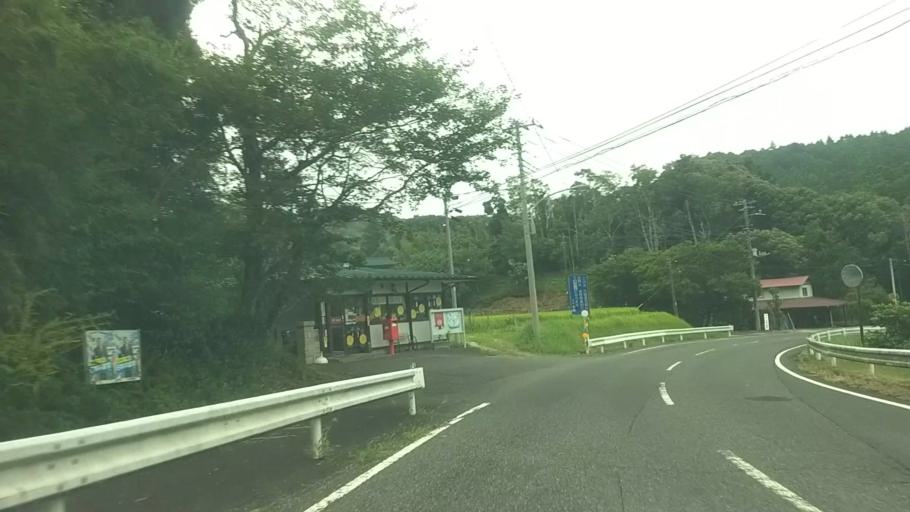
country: JP
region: Chiba
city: Kawaguchi
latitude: 35.2247
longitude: 140.0184
